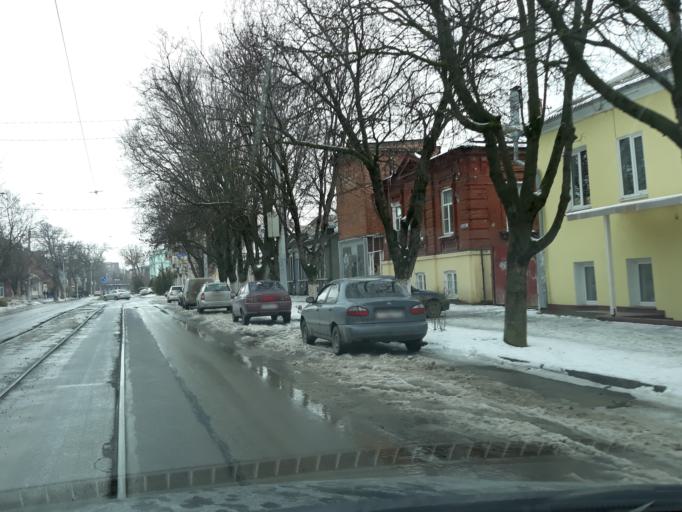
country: RU
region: Rostov
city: Taganrog
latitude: 47.2117
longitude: 38.9317
